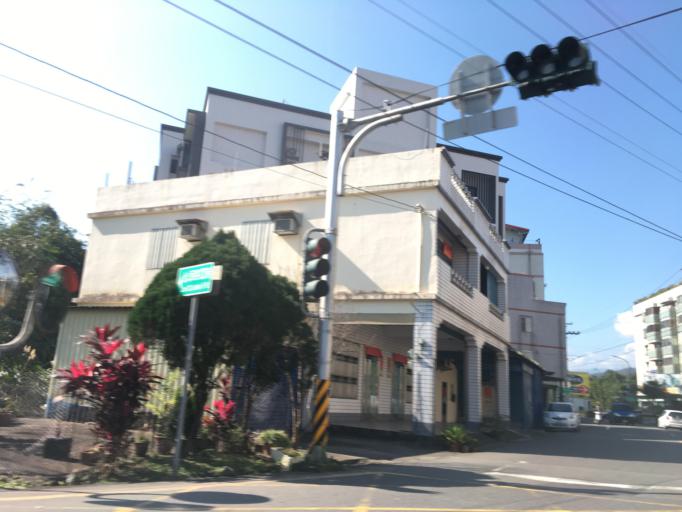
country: TW
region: Taiwan
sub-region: Yilan
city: Yilan
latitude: 24.7487
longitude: 121.7252
